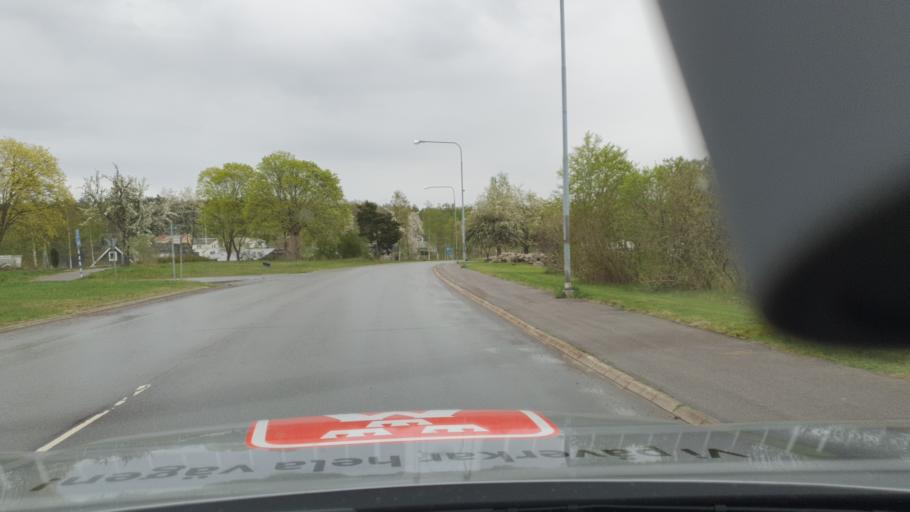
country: SE
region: Kalmar
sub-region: Vimmerby Kommun
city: Vimmerby
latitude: 57.6789
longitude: 15.8616
